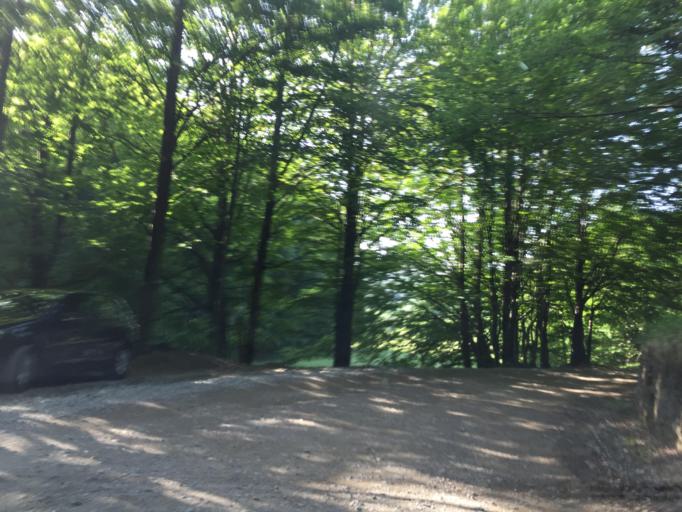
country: HR
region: Primorsko-Goranska
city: Klana
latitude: 45.4728
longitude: 14.4008
